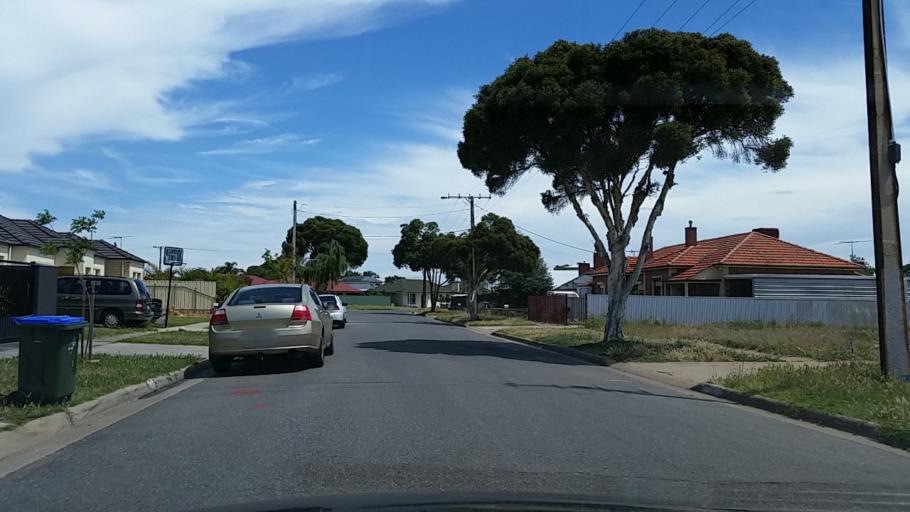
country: AU
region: South Australia
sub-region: Charles Sturt
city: Woodville West
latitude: -34.8854
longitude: 138.5245
